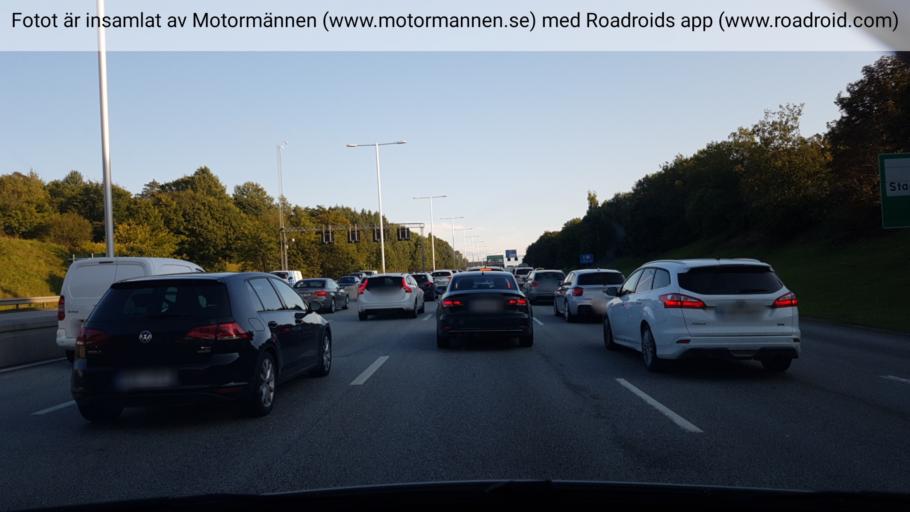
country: SE
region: Stockholm
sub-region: Solna Kommun
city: Solna
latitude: 59.3874
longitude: 18.0020
